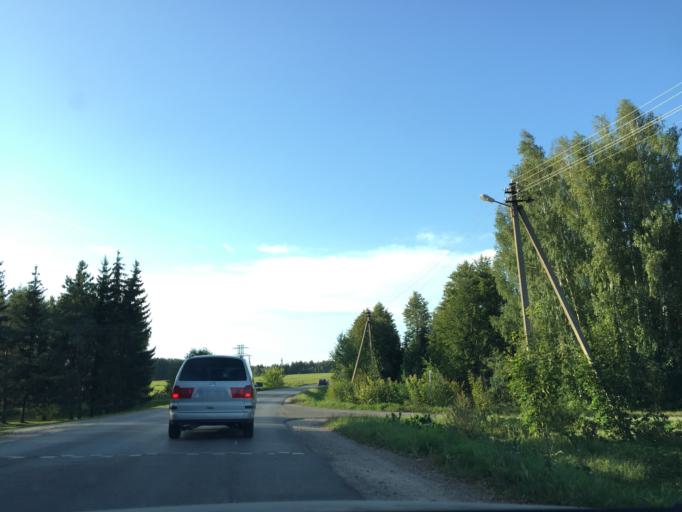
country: LT
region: Panevezys
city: Rokiskis
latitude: 55.9110
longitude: 25.6291
